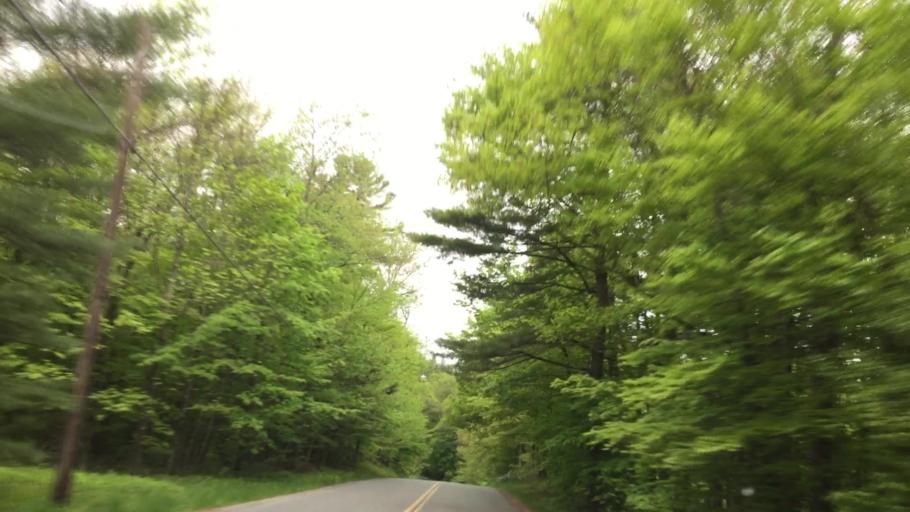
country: US
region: Massachusetts
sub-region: Berkshire County
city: Becket
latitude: 42.2768
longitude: -73.0375
